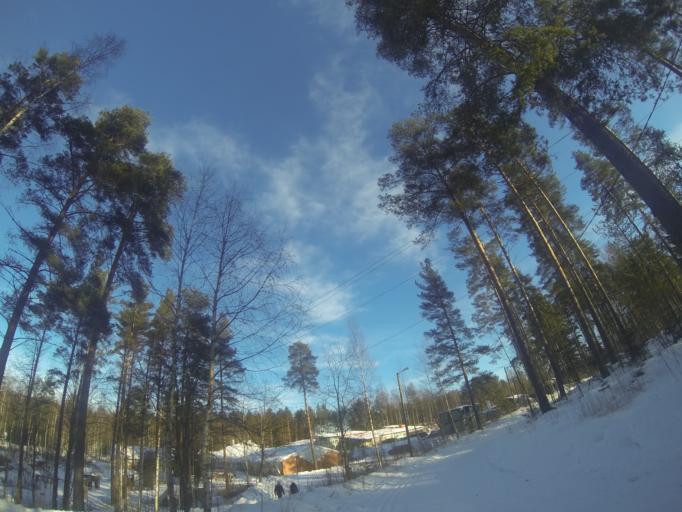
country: FI
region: Southern Savonia
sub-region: Savonlinna
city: Savonlinna
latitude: 61.8773
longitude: 28.9326
